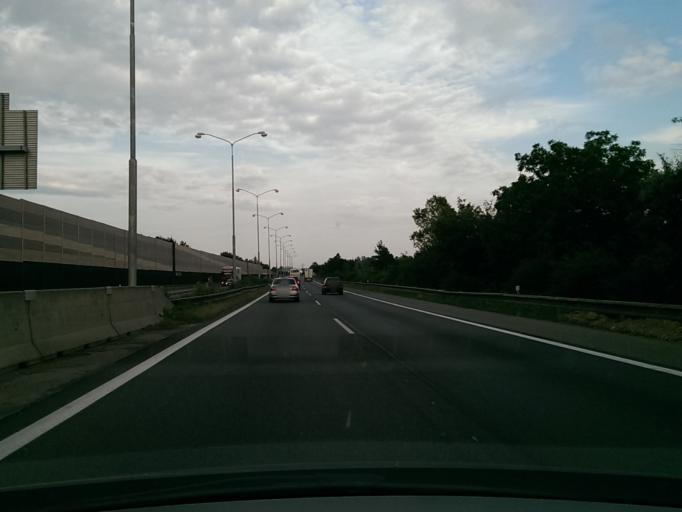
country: CZ
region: South Moravian
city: Ostopovice
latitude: 49.1658
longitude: 16.5504
